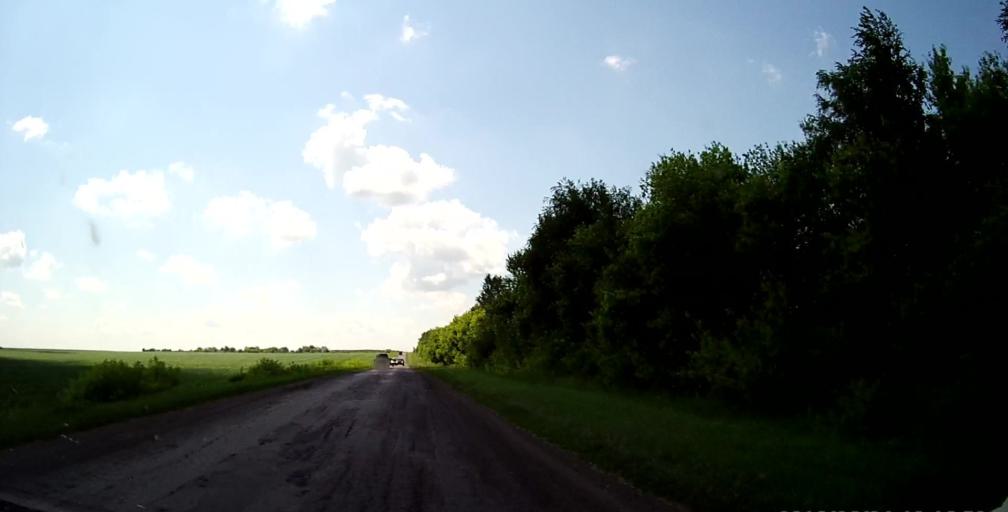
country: RU
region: Lipetsk
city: Chaplygin
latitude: 53.2818
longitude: 39.9614
